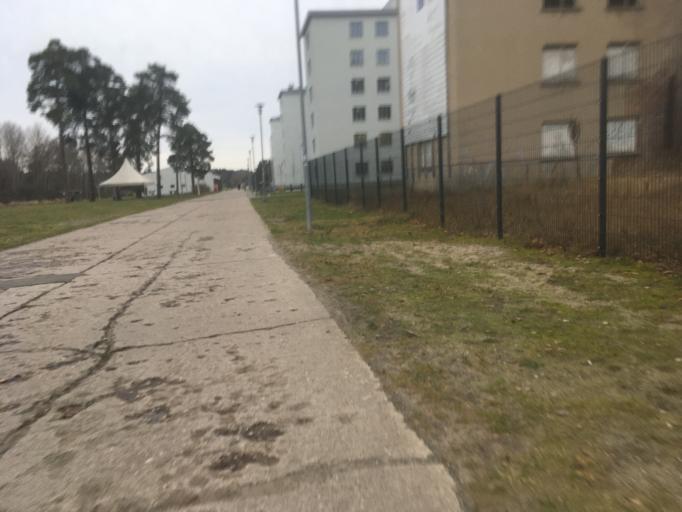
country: DE
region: Mecklenburg-Vorpommern
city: Ostseebad Binz
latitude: 54.4500
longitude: 13.5696
